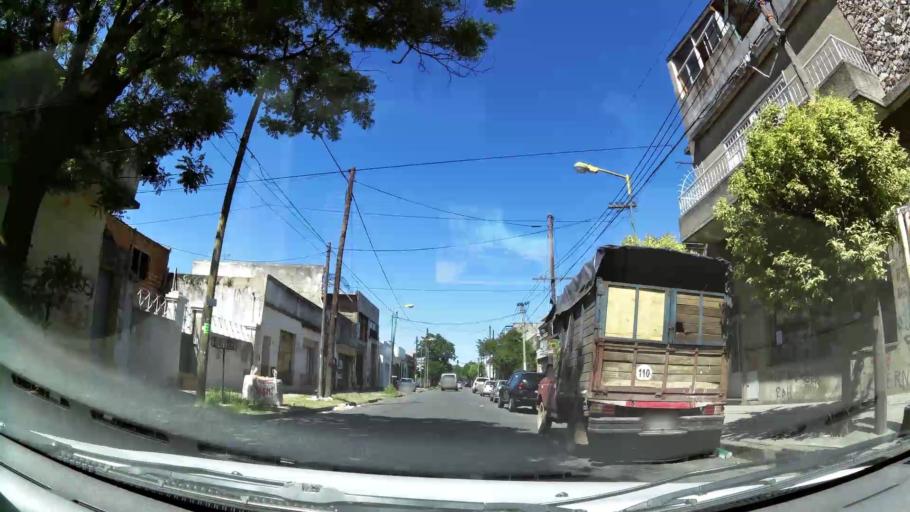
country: AR
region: Buenos Aires
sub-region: Partido de General San Martin
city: General San Martin
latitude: -34.5831
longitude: -58.5459
